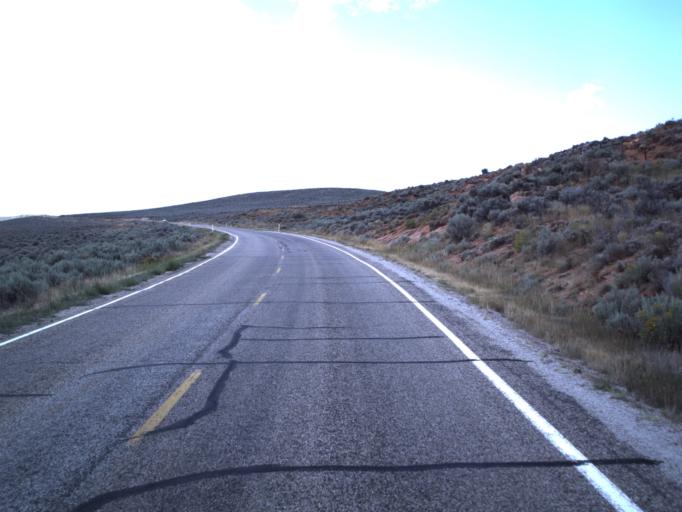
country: US
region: Utah
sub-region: Rich County
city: Randolph
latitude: 41.7906
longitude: -111.2149
